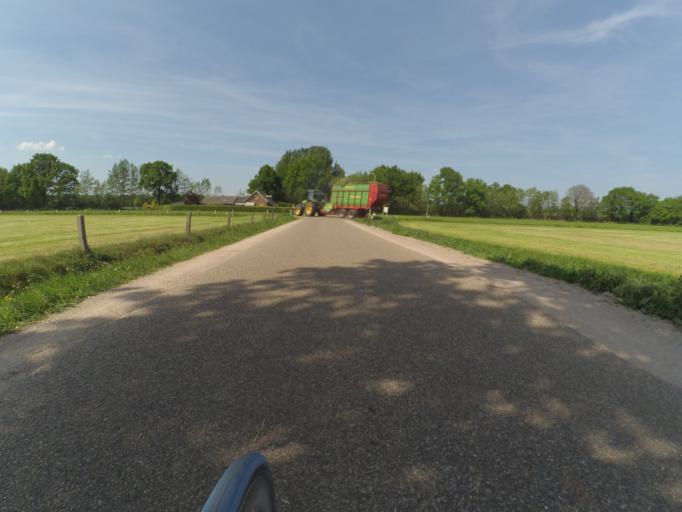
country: NL
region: Overijssel
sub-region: Gemeente Tubbergen
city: Tubbergen
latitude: 52.3582
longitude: 6.7986
